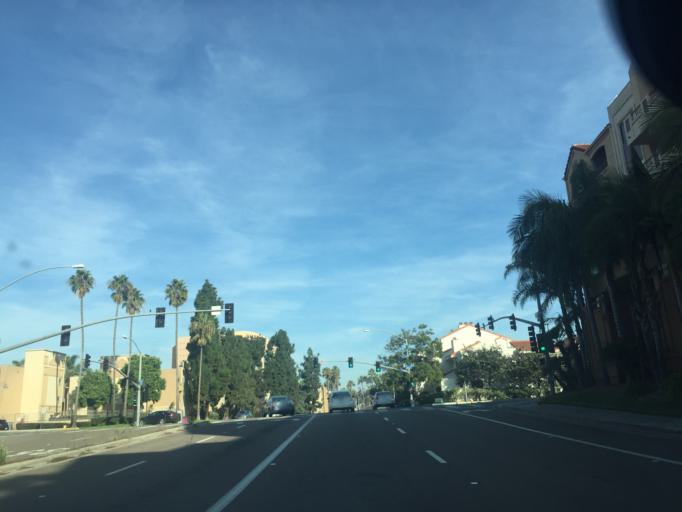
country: US
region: California
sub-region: San Diego County
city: La Jolla
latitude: 32.8679
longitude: -117.2248
